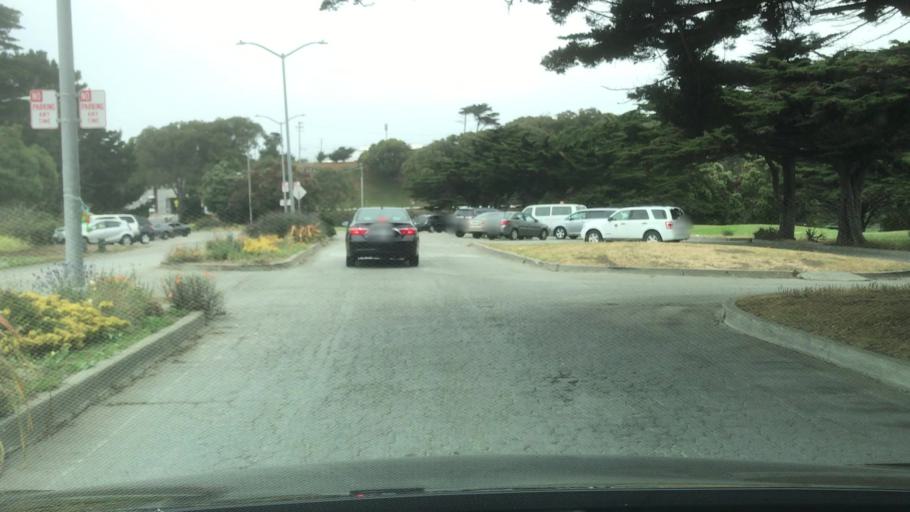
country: US
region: California
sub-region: San Mateo County
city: Daly City
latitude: 37.7262
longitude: -122.4998
